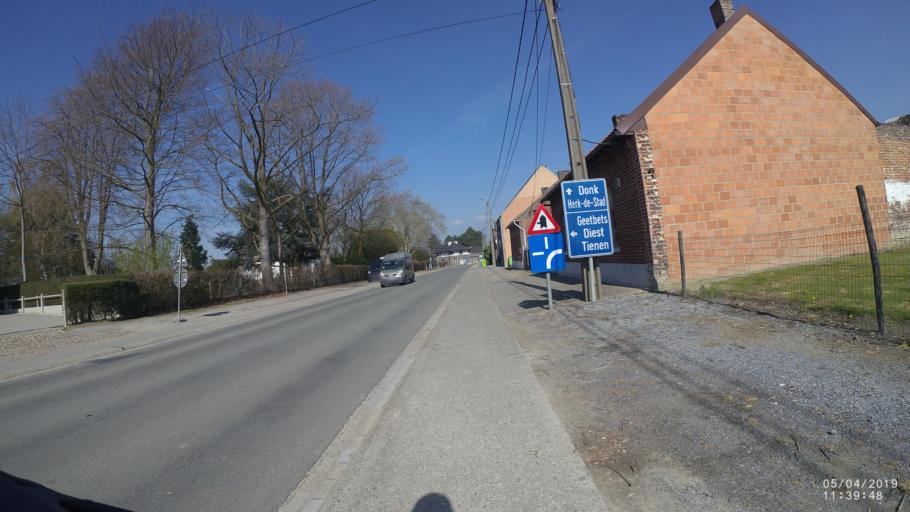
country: BE
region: Flanders
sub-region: Provincie Limburg
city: Herk-de-Stad
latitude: 50.8944
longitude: 5.1596
